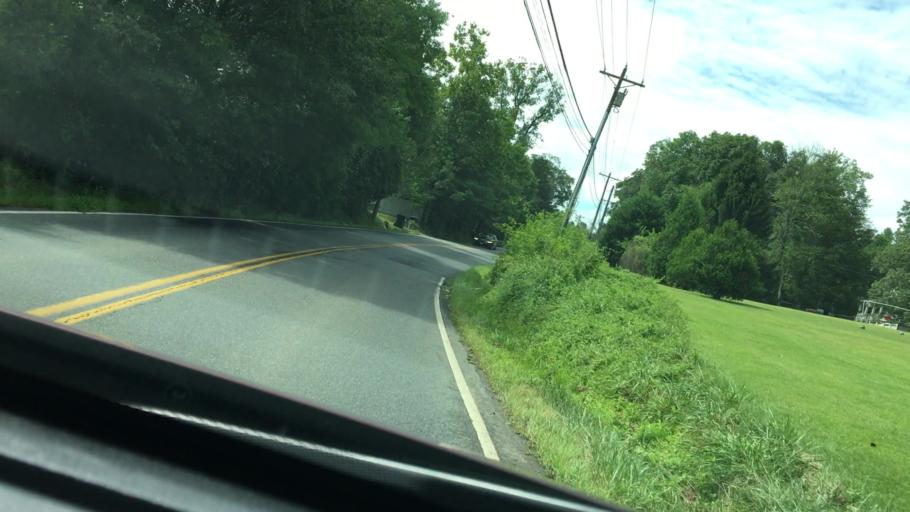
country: US
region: Virginia
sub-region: Prince William County
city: Buckhall
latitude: 38.7444
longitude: -77.4370
